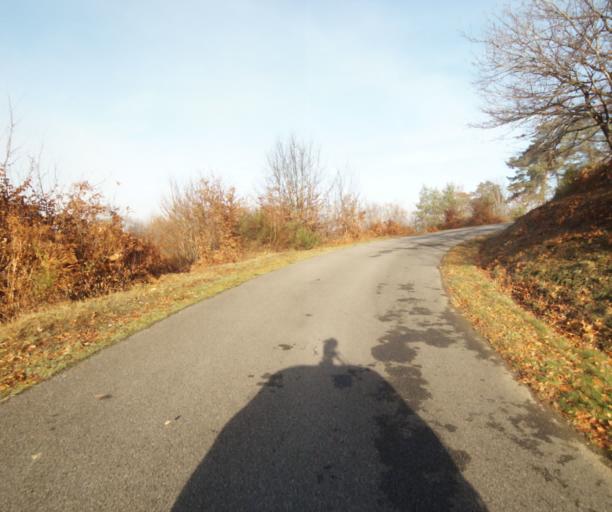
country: FR
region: Limousin
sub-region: Departement de la Correze
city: Laguenne
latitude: 45.2607
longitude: 1.7917
